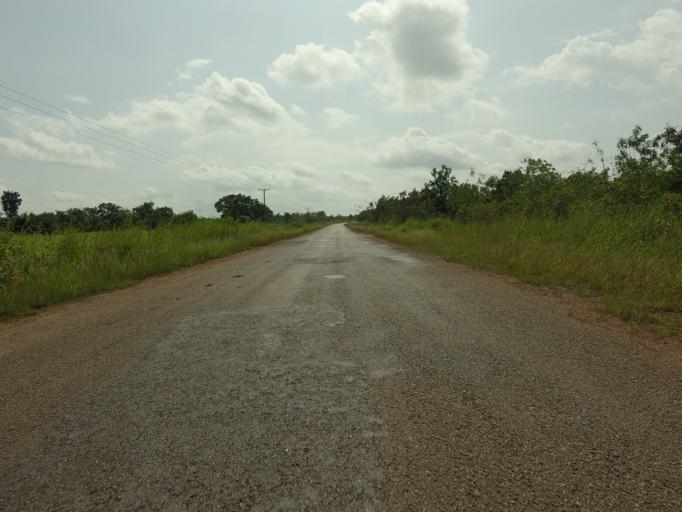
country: TG
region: Maritime
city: Lome
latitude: 6.2590
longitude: 0.9602
